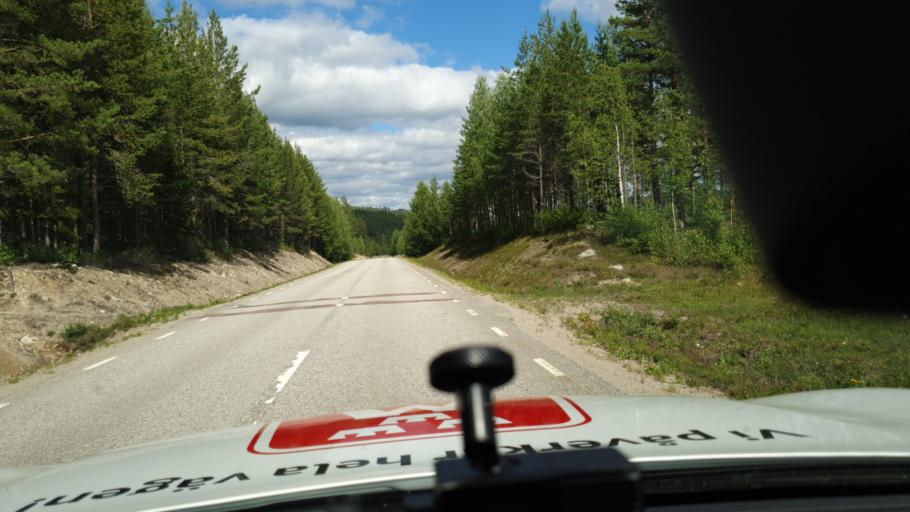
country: NO
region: Hedmark
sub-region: Trysil
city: Innbygda
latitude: 61.0202
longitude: 12.5402
